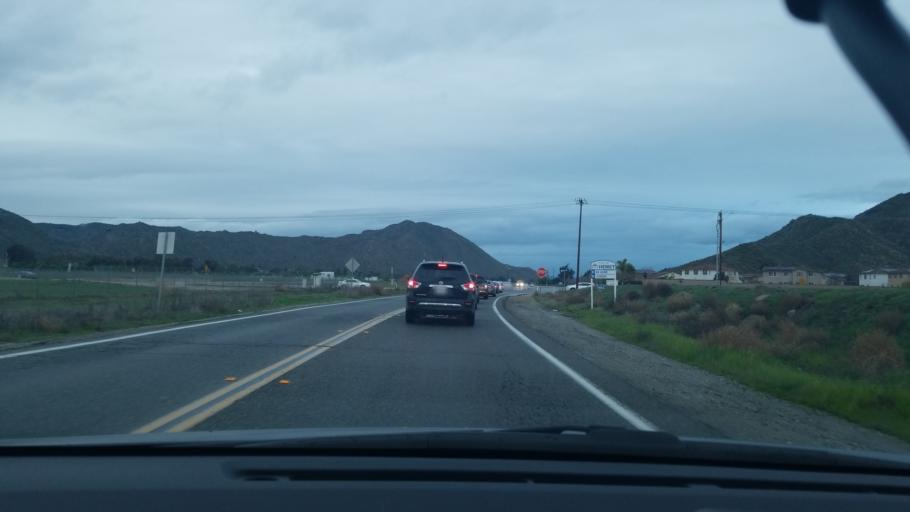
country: US
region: California
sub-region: Riverside County
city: Green Acres
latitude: 33.7502
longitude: -117.0360
